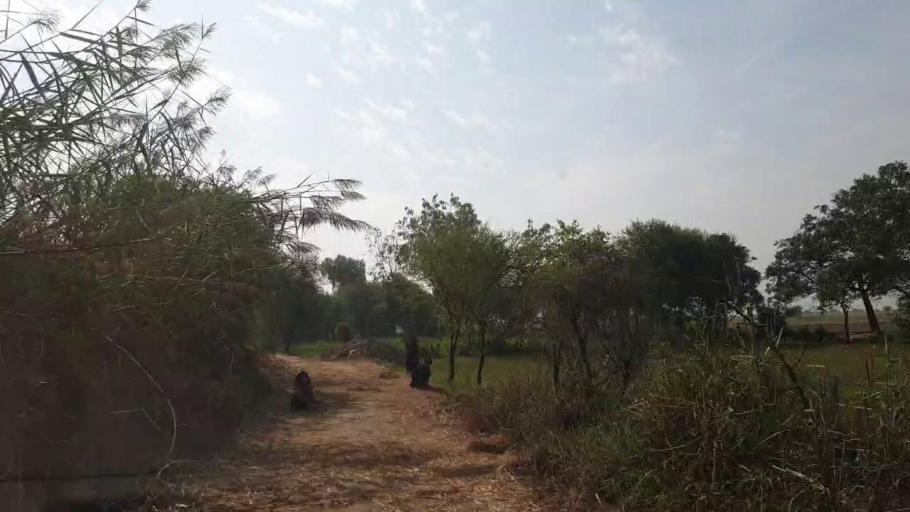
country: PK
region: Sindh
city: Tando Bago
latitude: 24.8832
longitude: 69.0034
